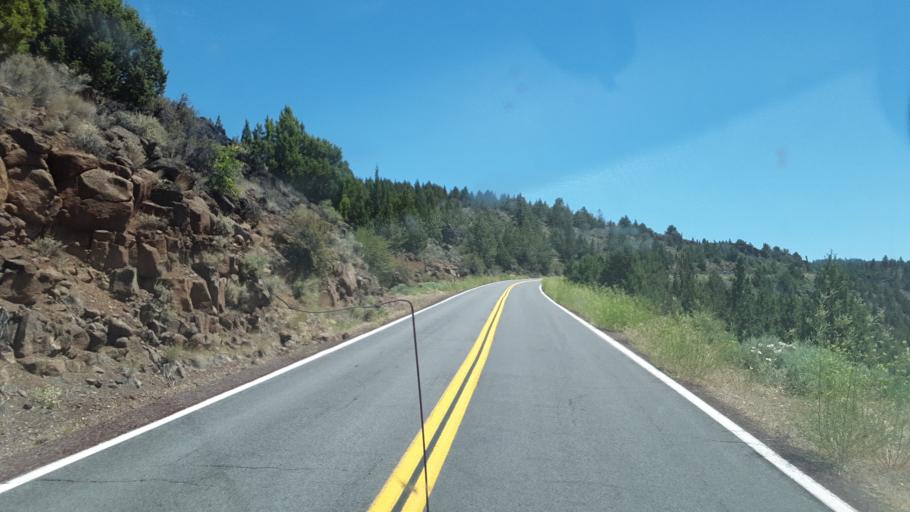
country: US
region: California
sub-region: Lassen County
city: Susanville
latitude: 40.6476
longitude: -120.6574
